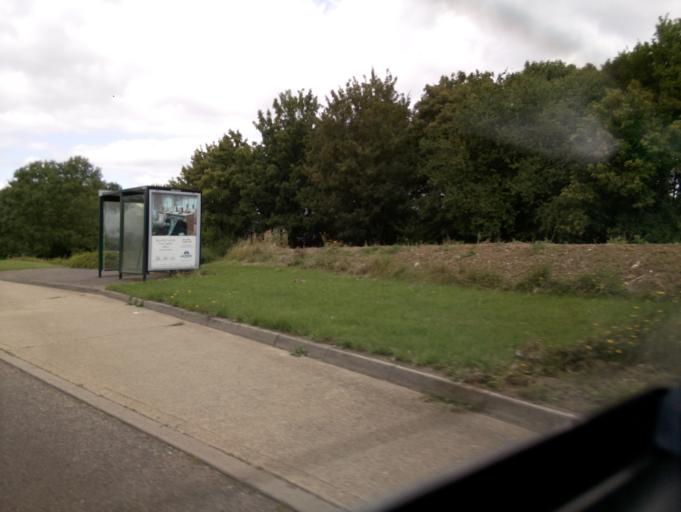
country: GB
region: England
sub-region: Milton Keynes
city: Shenley Church End
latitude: 52.0208
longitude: -0.8000
